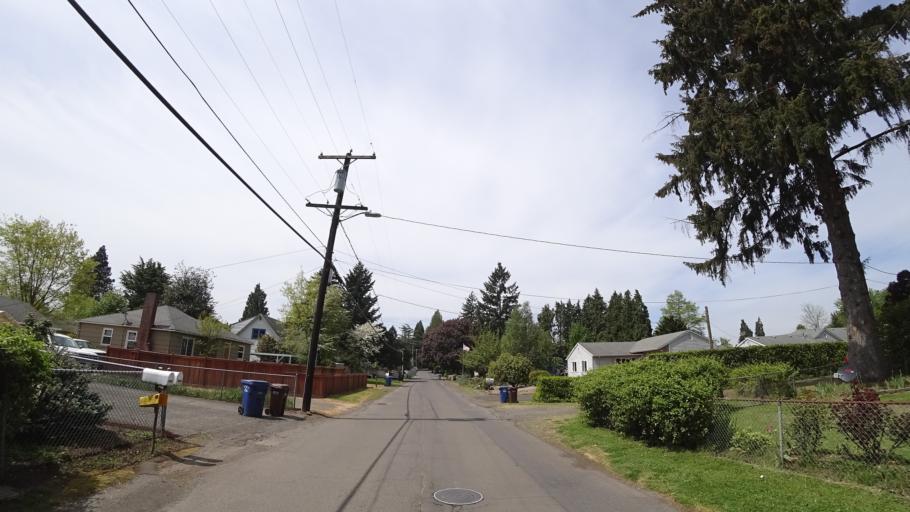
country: US
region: Oregon
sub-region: Clackamas County
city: Milwaukie
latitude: 45.4505
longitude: -122.6158
